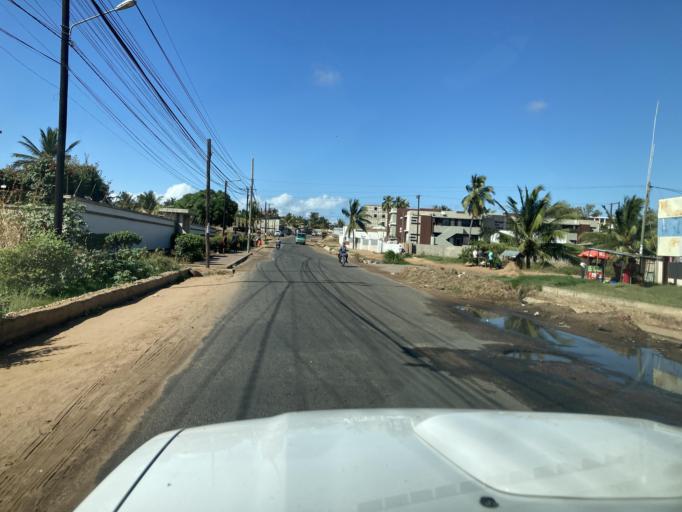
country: MZ
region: Cabo Delgado
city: Pemba
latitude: -12.9756
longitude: 40.5411
